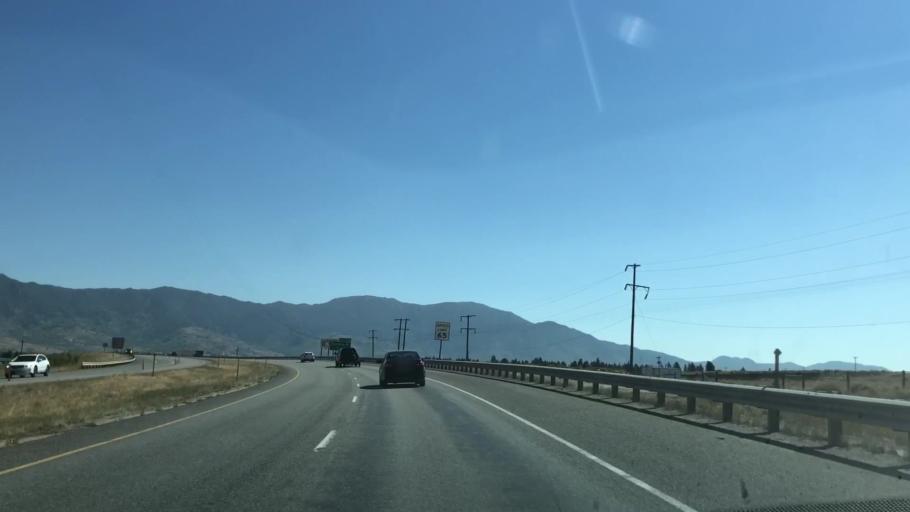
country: US
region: Montana
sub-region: Silver Bow County
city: Butte
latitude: 45.9927
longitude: -112.5548
